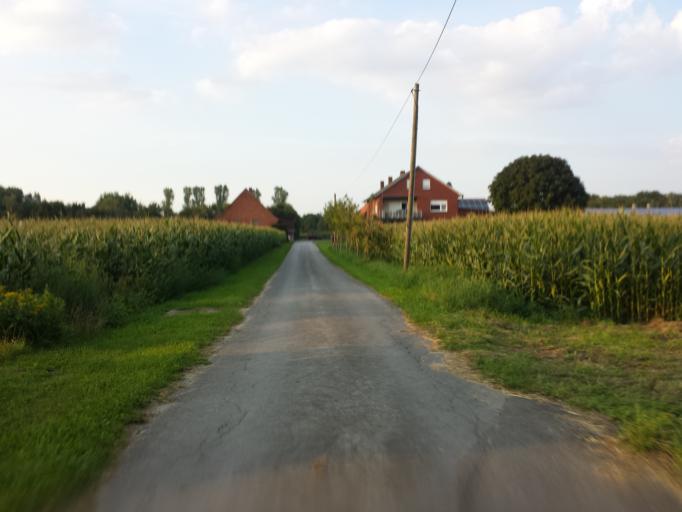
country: DE
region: North Rhine-Westphalia
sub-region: Regierungsbezirk Detmold
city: Guetersloh
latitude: 51.9310
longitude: 8.3161
